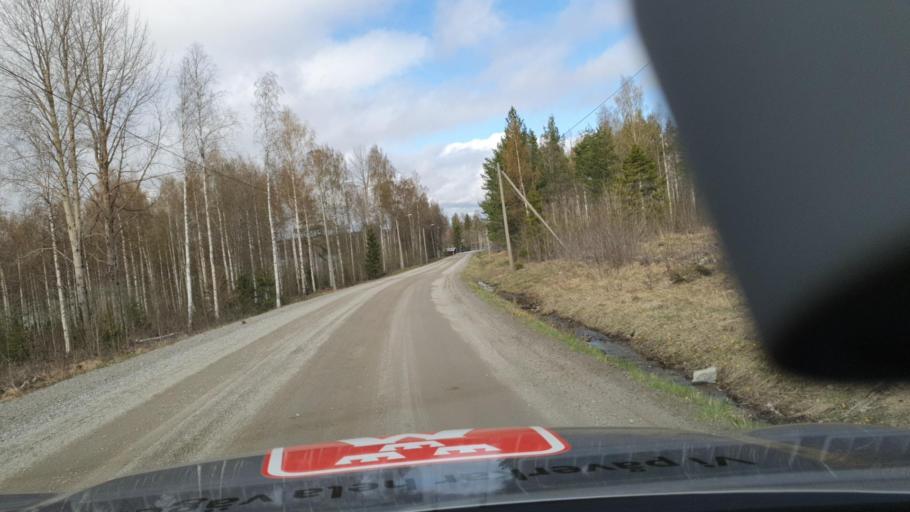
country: SE
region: Vaesterbotten
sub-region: Bjurholms Kommun
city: Bjurholm
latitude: 63.6882
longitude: 18.9589
